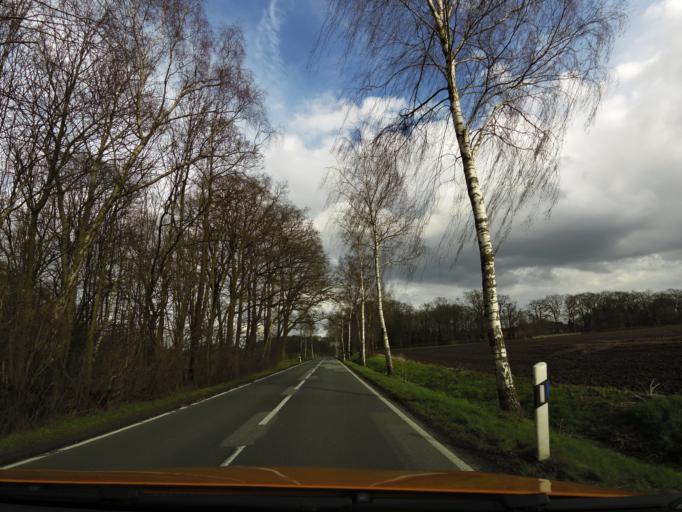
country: DE
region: Lower Saxony
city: Dunsen
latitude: 52.8933
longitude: 8.6586
